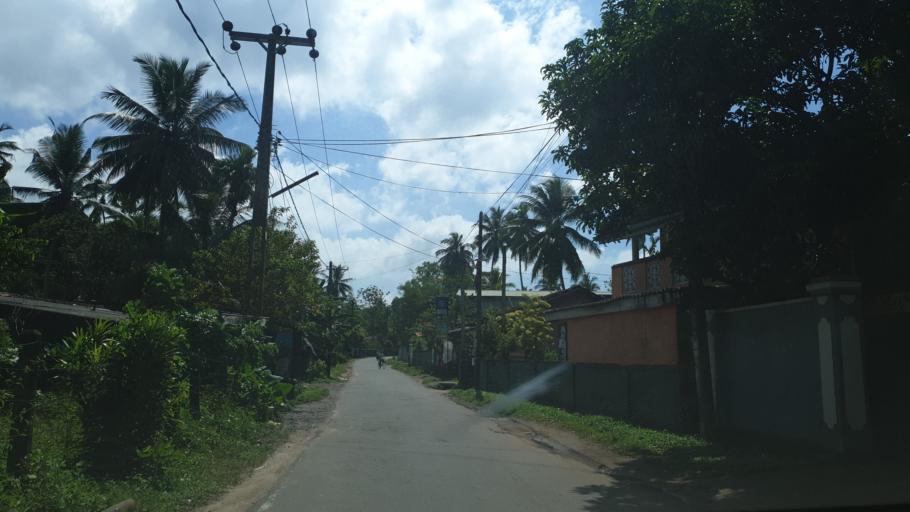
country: LK
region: Western
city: Panadura
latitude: 6.6814
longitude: 79.9292
